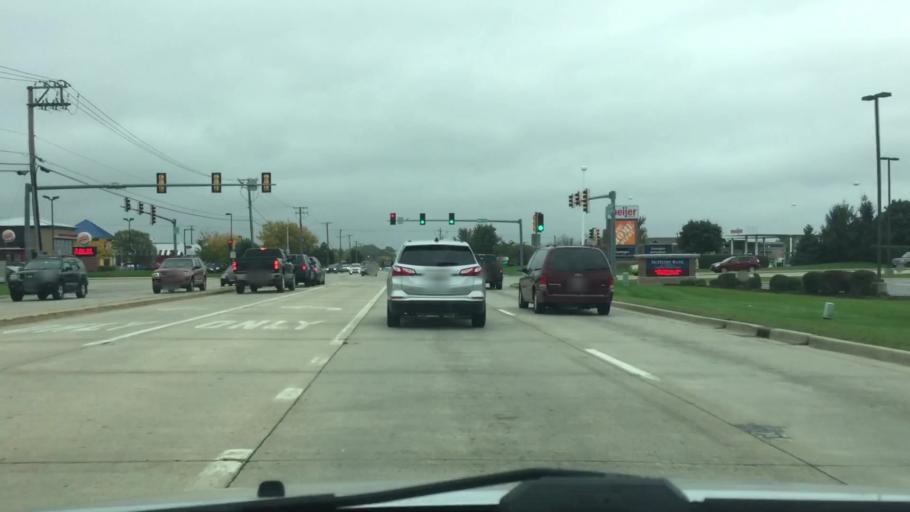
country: US
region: Illinois
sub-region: McHenry County
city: McHenry
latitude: 42.3596
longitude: -88.2674
